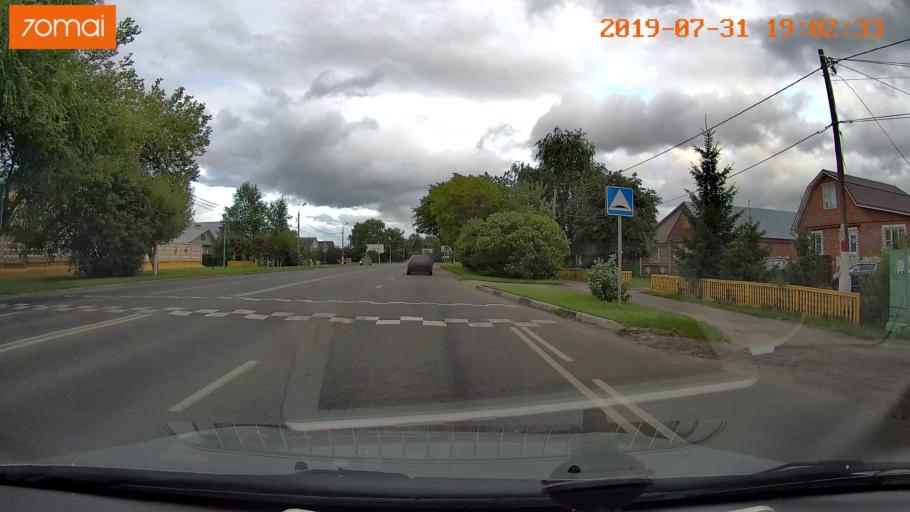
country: RU
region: Moskovskaya
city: Raduzhnyy
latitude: 55.1196
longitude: 38.7332
